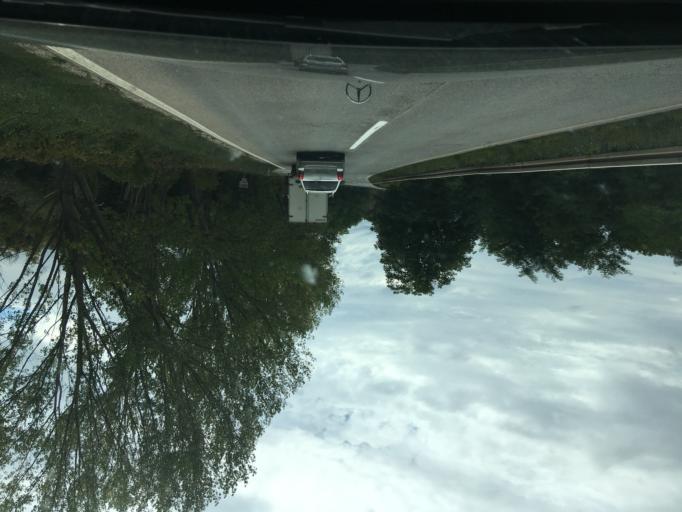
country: RS
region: Central Serbia
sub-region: Pirotski Okrug
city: Bela Palanka
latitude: 43.2810
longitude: 22.2227
